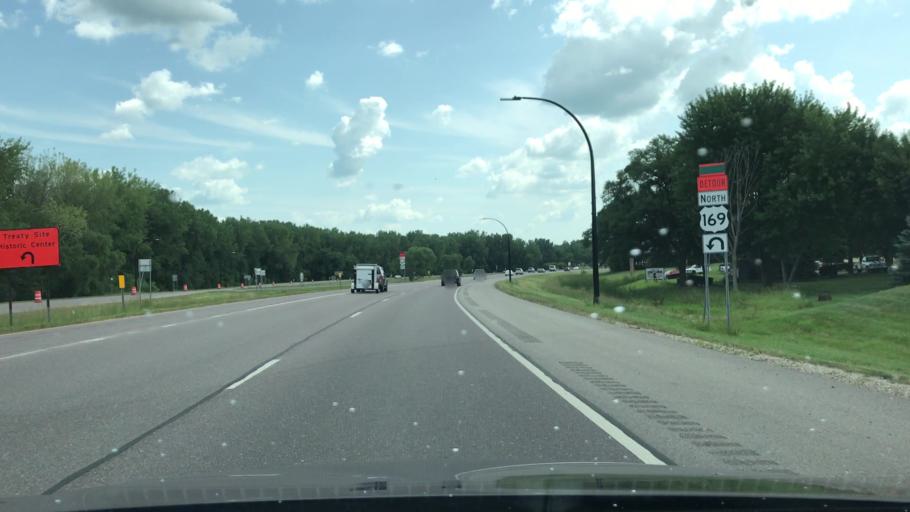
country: US
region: Minnesota
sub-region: Nicollet County
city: Saint Peter
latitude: 44.3391
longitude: -93.9483
